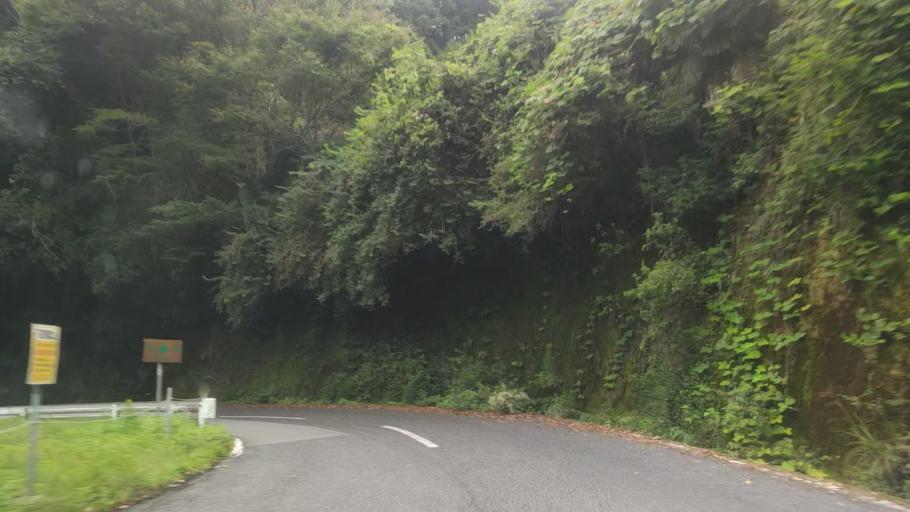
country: JP
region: Wakayama
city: Koya
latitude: 34.2455
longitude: 135.5457
